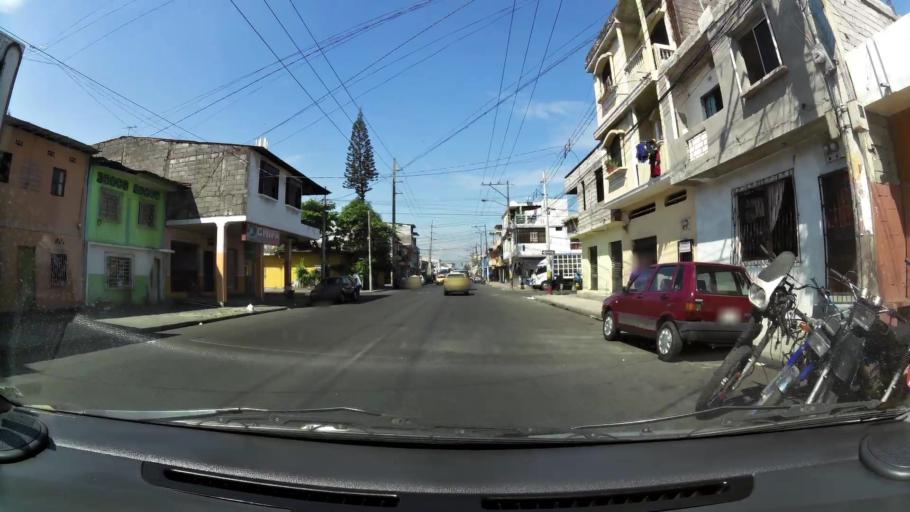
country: EC
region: Guayas
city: Guayaquil
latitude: -2.2103
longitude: -79.9089
